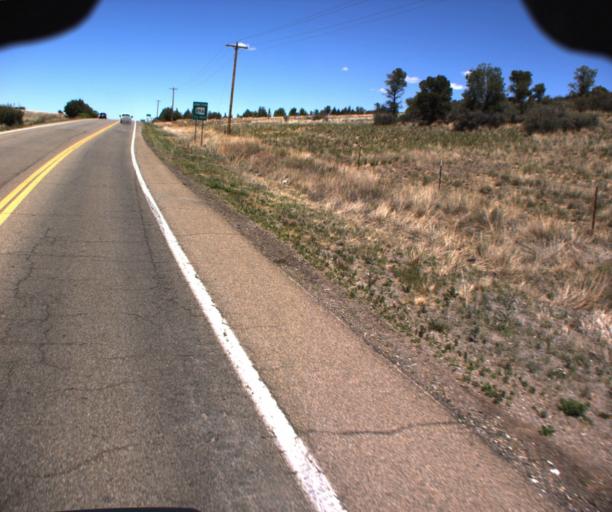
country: US
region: Arizona
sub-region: Yavapai County
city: Prescott
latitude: 34.6242
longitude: -112.4266
